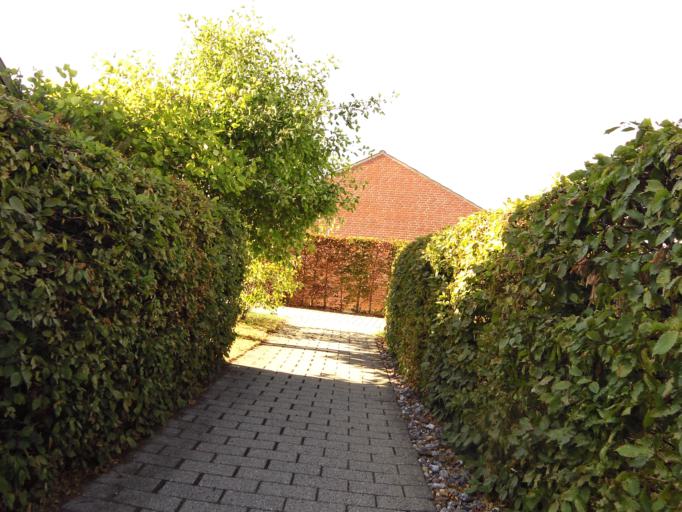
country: DK
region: Capital Region
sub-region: Fredensborg Kommune
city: Niva
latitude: 55.9437
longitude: 12.5071
